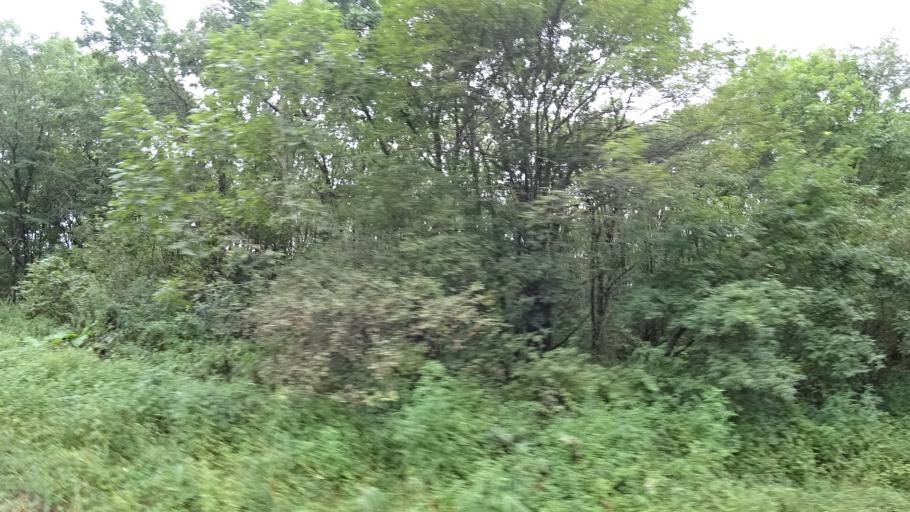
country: RU
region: Primorskiy
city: Rettikhovka
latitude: 44.0592
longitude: 132.6544
